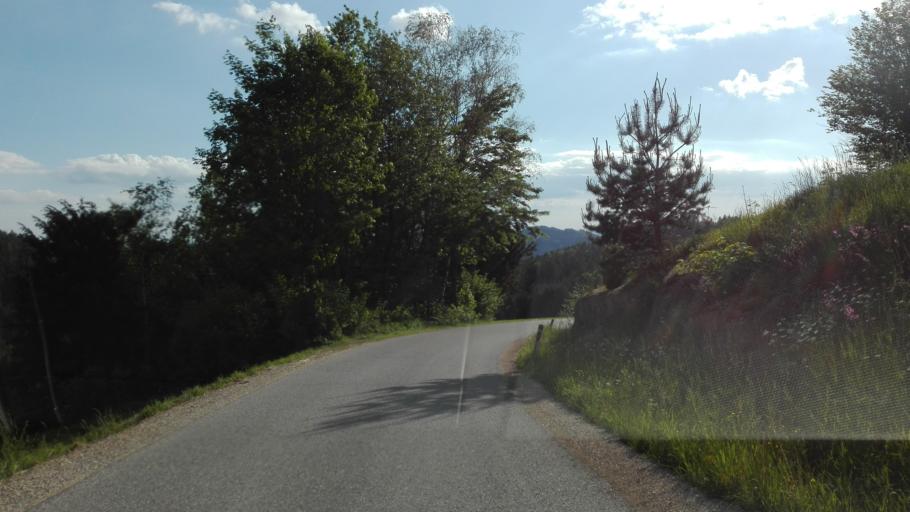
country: AT
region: Upper Austria
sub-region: Politischer Bezirk Perg
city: Perg
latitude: 48.4055
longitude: 14.6740
